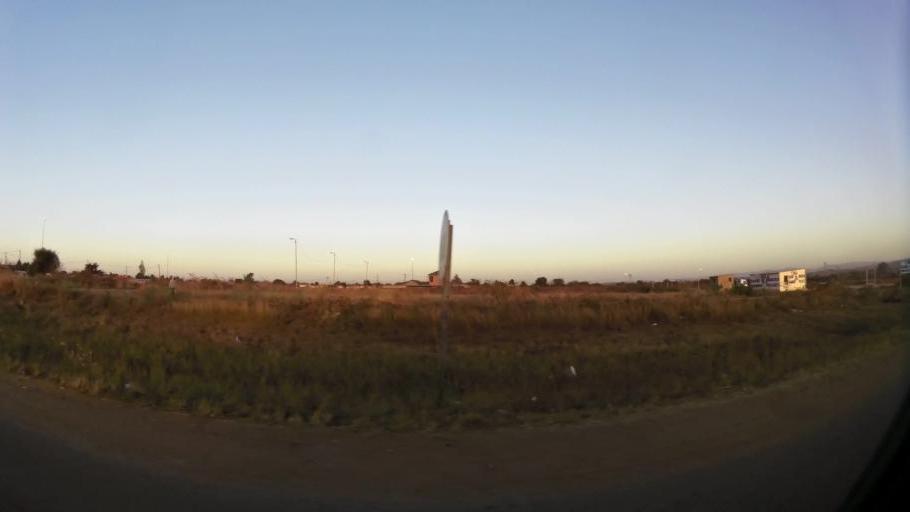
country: ZA
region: North-West
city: Ga-Rankuwa
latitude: -25.5714
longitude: 28.0525
